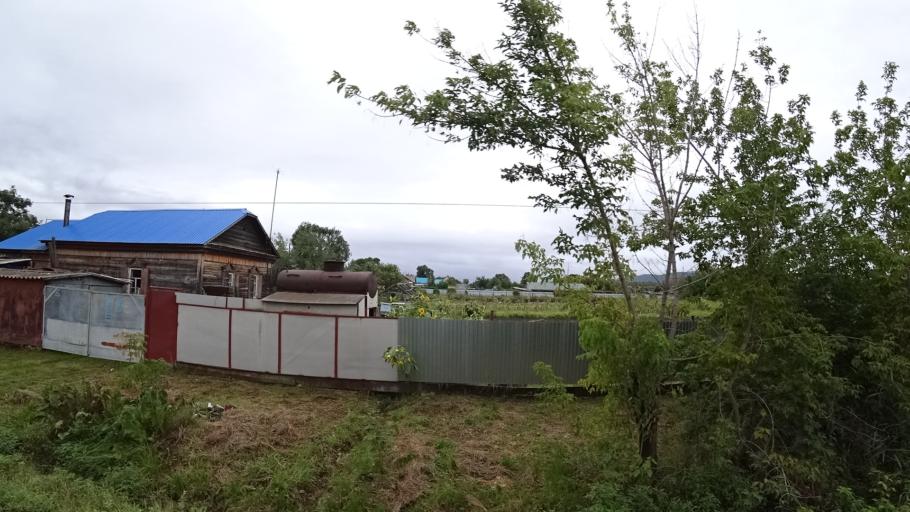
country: RU
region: Primorskiy
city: Chernigovka
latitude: 44.3394
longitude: 132.5670
